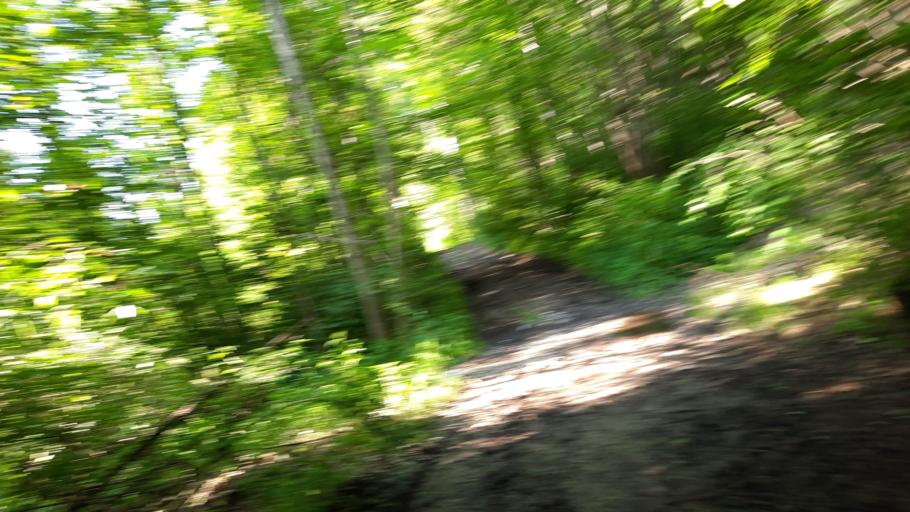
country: DE
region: Bavaria
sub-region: Upper Bavaria
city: Glonn
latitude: 47.9591
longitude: 11.9041
